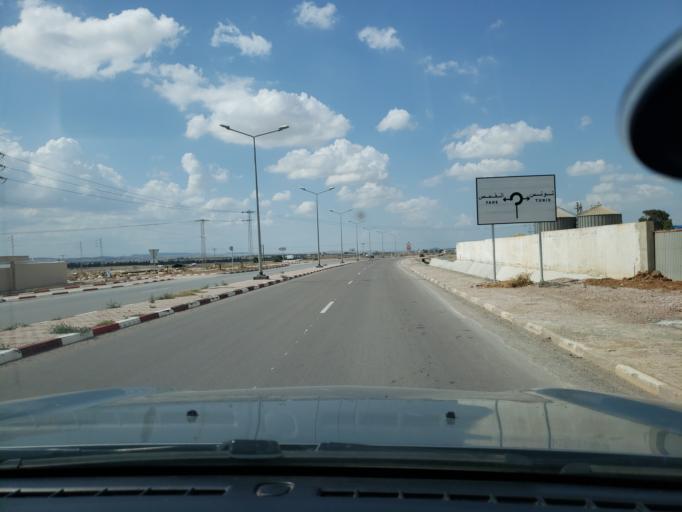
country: TN
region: Tunis
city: La Mohammedia
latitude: 36.5624
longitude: 10.0838
